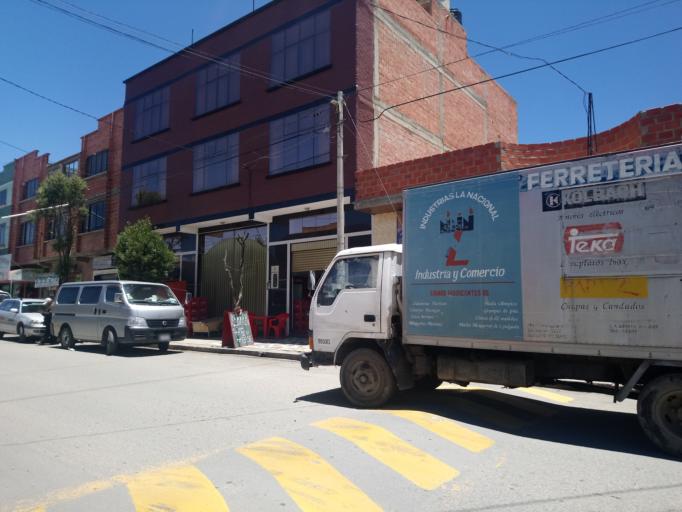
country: BO
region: La Paz
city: La Paz
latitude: -16.5470
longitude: -68.1903
